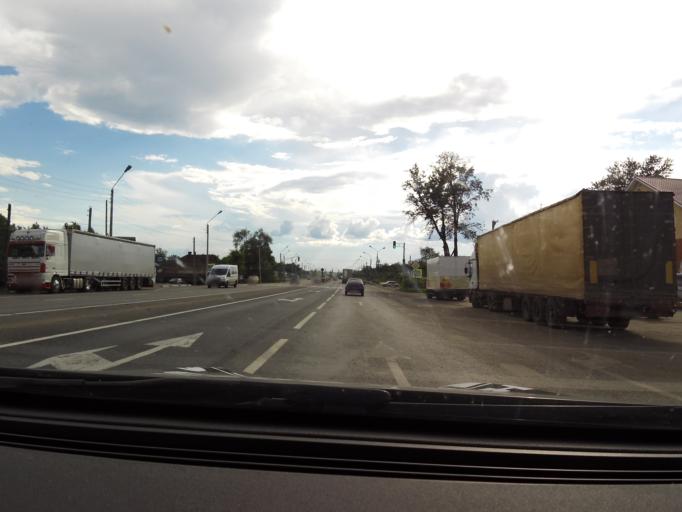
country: RU
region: Vladimir
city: Galitsy
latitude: 56.2291
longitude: 42.7984
